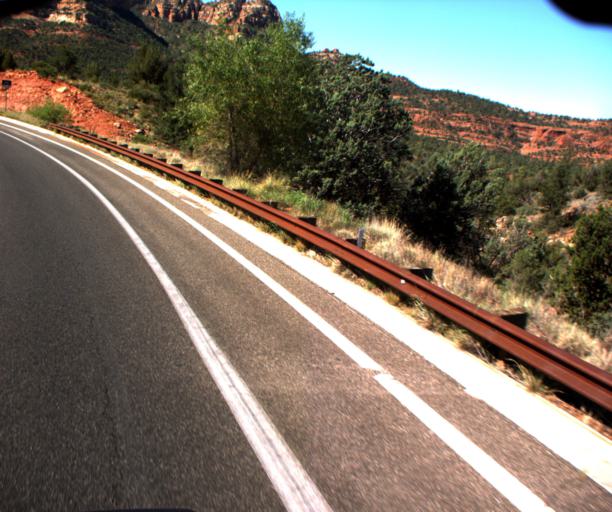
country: US
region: Arizona
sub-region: Yavapai County
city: Village of Oak Creek (Big Park)
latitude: 34.8208
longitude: -111.7752
